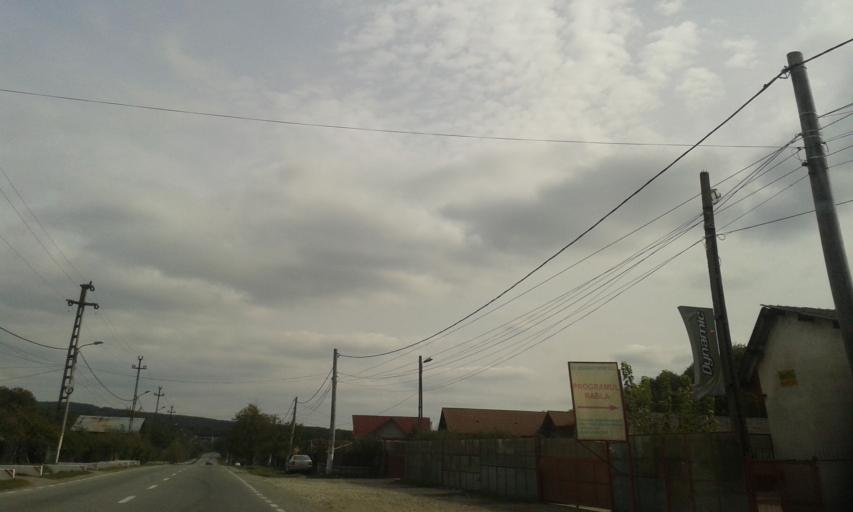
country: RO
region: Gorj
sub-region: Comuna Balanesti
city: Balanesti
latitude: 45.0413
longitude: 23.3539
